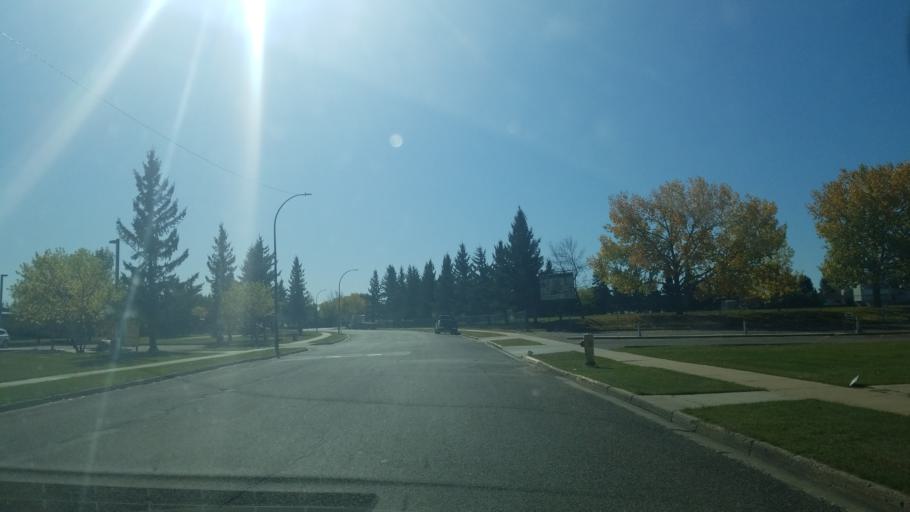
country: CA
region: Saskatchewan
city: Lloydminster
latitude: 53.2751
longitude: -110.0198
